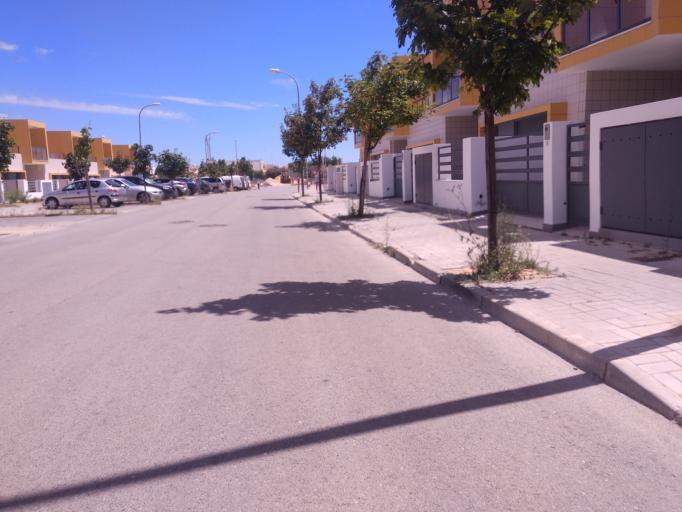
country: PT
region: Faro
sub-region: Sao Bras de Alportel
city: Sao Bras de Alportel
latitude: 37.1549
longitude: -7.8842
